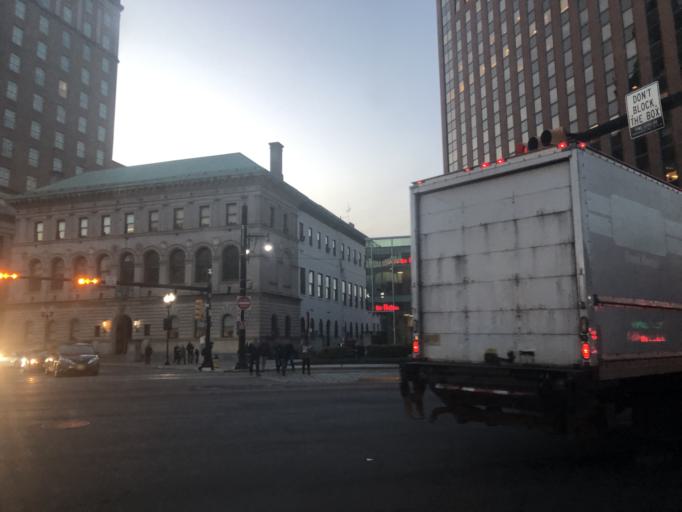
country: US
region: New Jersey
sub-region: Hudson County
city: East Newark
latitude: 40.7446
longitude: -74.1696
